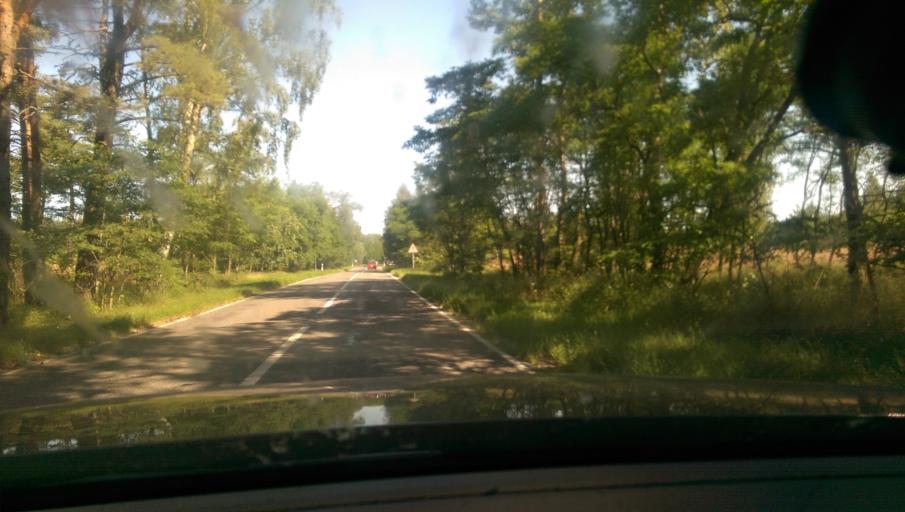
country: LT
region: Klaipedos apskritis
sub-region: Klaipeda
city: Klaipeda
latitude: 55.6819
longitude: 21.1135
